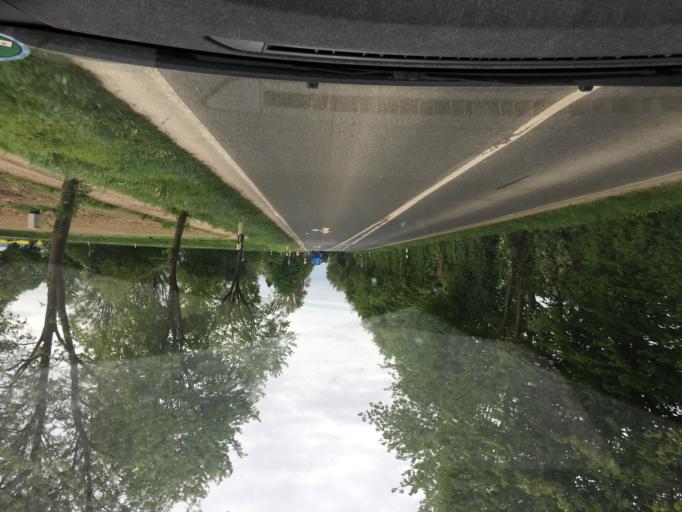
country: DE
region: North Rhine-Westphalia
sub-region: Regierungsbezirk Koln
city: Titz
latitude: 51.0558
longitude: 6.4286
